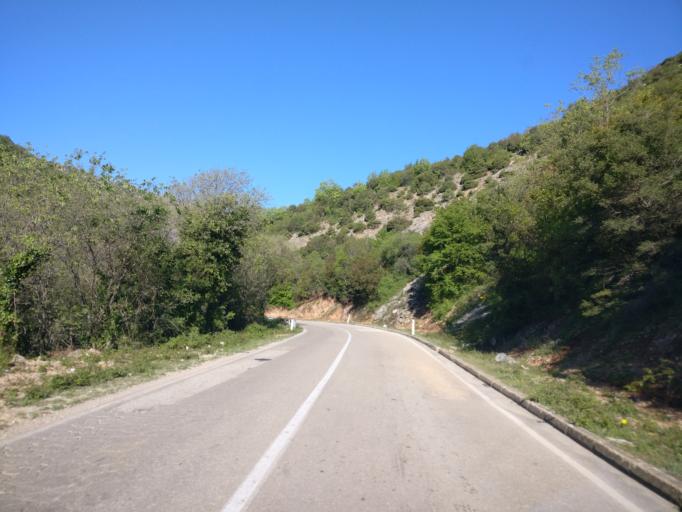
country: BA
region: Federation of Bosnia and Herzegovina
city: Stolac
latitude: 43.0722
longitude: 18.0528
